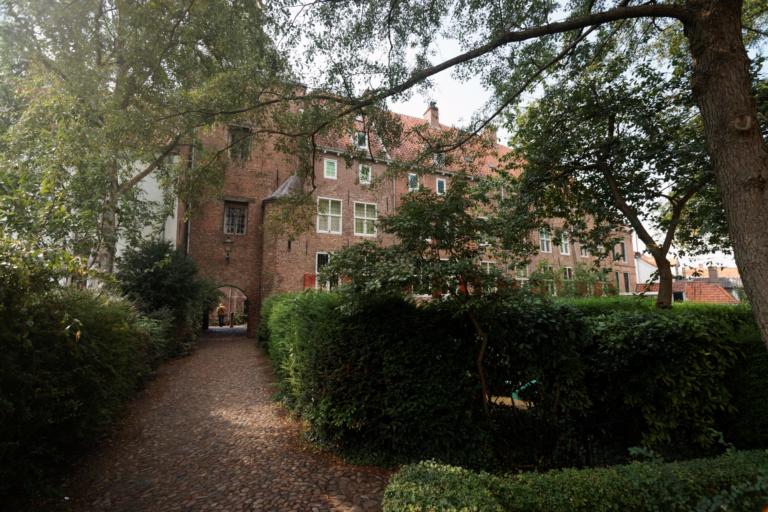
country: NL
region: Utrecht
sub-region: Gemeente Amersfoort
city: Amersfoort
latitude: 52.1561
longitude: 5.3932
